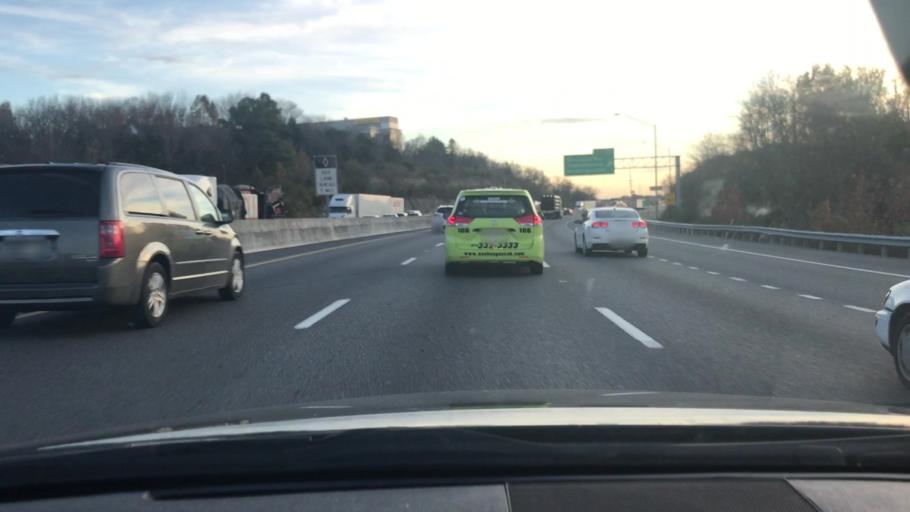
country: US
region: Tennessee
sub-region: Davidson County
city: Goodlettsville
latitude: 36.3127
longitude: -86.7015
